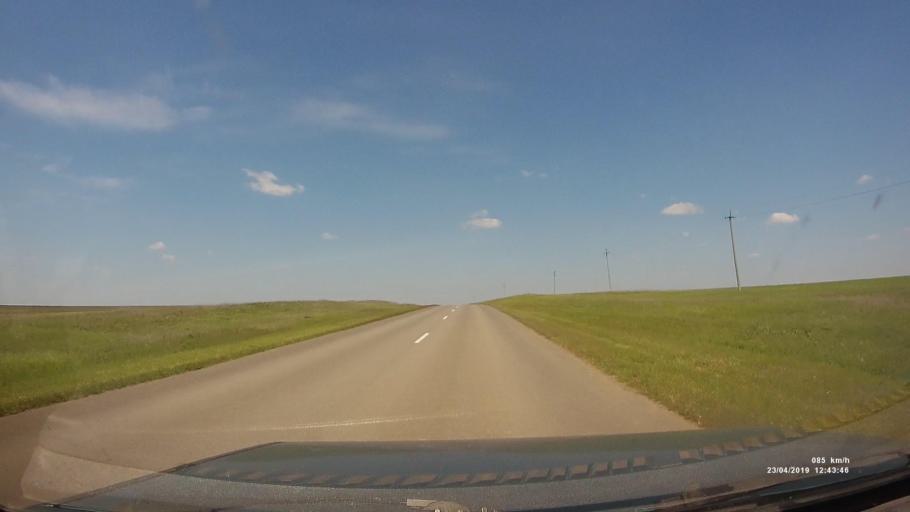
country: RU
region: Kalmykiya
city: Yashalta
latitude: 46.4683
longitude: 42.6501
